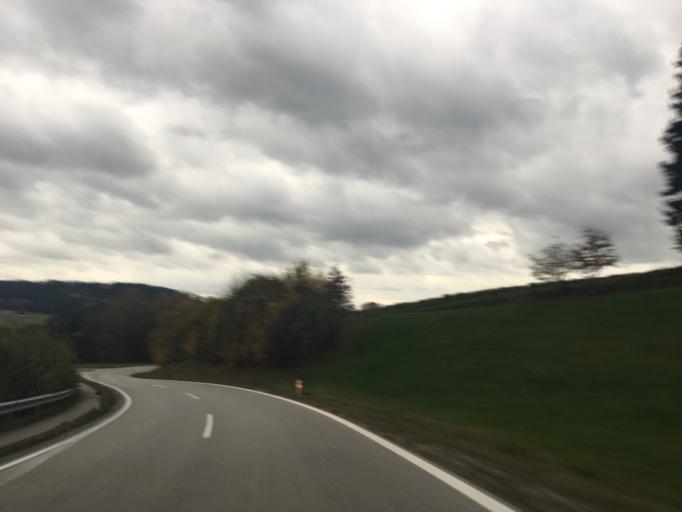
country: AT
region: Upper Austria
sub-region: Politischer Bezirk Rohrbach
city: Schlaegl
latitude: 48.5743
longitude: 14.0629
